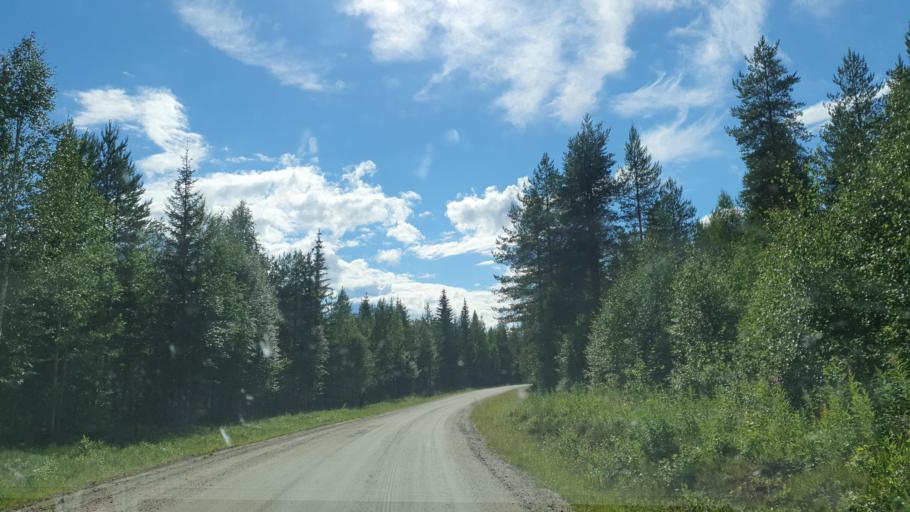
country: FI
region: Kainuu
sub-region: Kehys-Kainuu
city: Kuhmo
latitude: 64.1553
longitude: 29.8044
